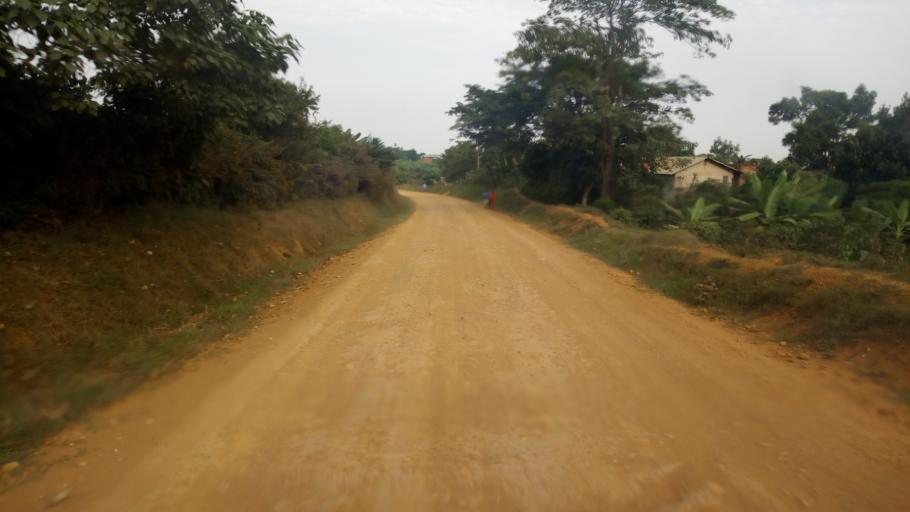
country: UG
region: Western Region
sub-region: Kanungu District
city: Ntungamo
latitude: -0.8279
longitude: 29.7019
